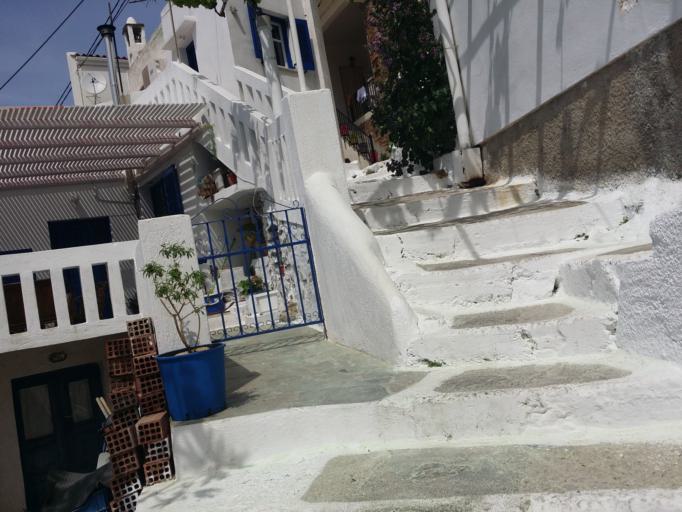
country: GR
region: South Aegean
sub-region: Nomos Kykladon
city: Kea
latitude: 37.6417
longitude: 24.3400
